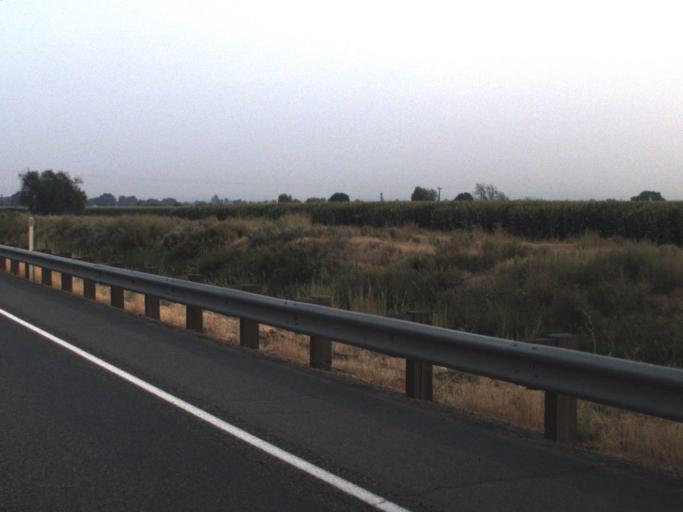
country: US
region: Washington
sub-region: Yakima County
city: Toppenish
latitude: 46.3433
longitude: -120.3205
